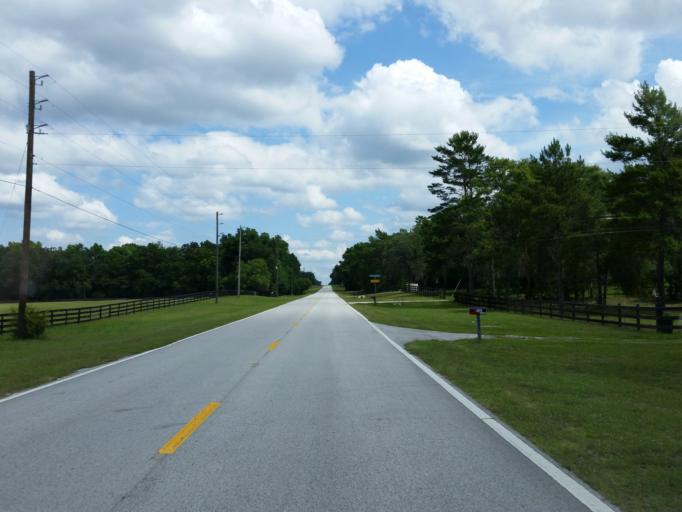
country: US
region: Florida
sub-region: Citrus County
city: Floral City
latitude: 28.6680
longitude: -82.3599
